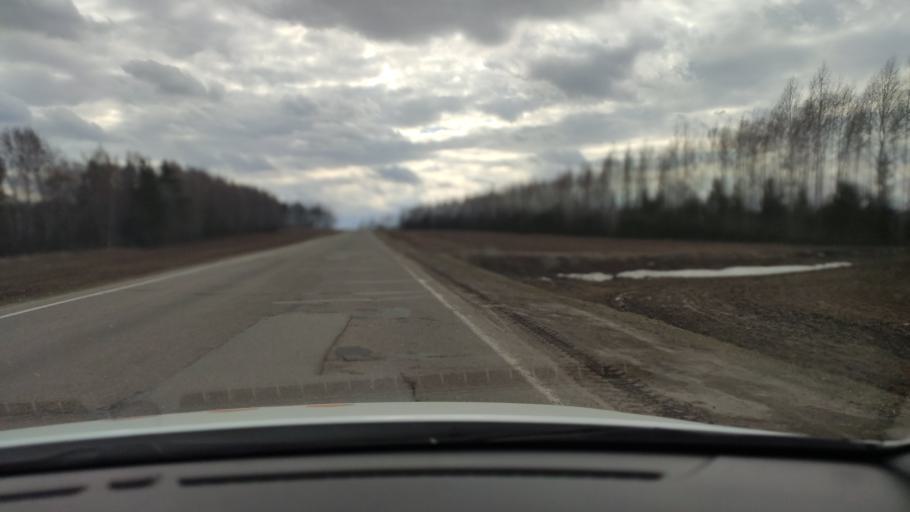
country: RU
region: Tatarstan
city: Vysokaya Gora
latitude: 56.1078
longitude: 49.1785
